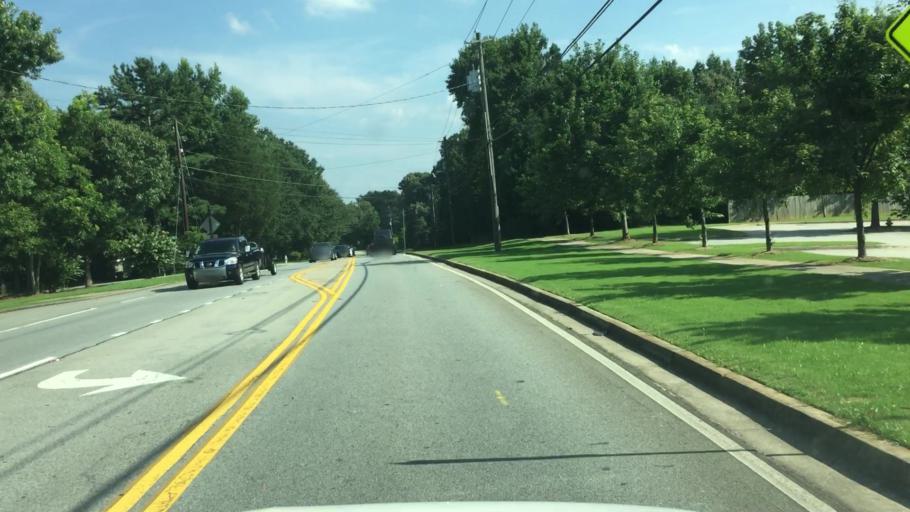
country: US
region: Georgia
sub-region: Gwinnett County
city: Dacula
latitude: 33.9797
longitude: -83.8939
